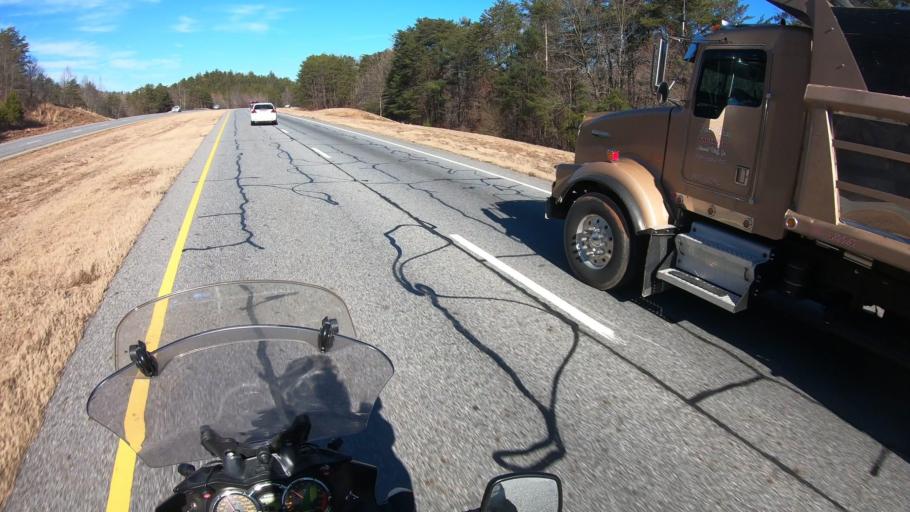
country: US
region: Georgia
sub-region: Gilmer County
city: Ellijay
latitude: 34.7537
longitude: -84.4067
